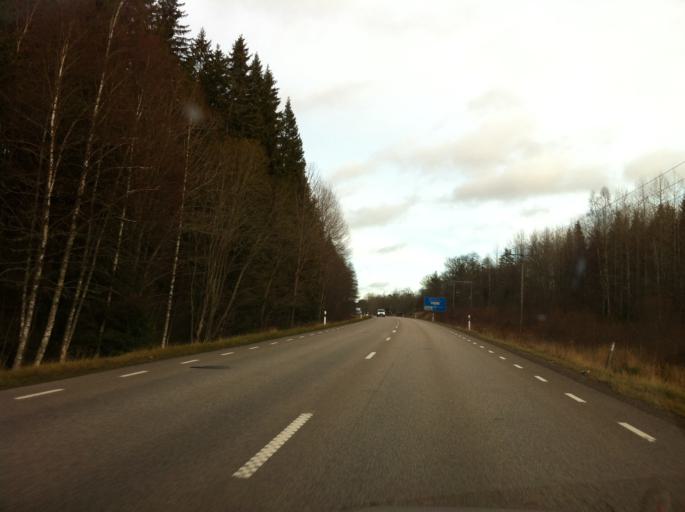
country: SE
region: Kronoberg
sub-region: Uppvidinge Kommun
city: Aseda
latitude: 57.1260
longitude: 15.2677
